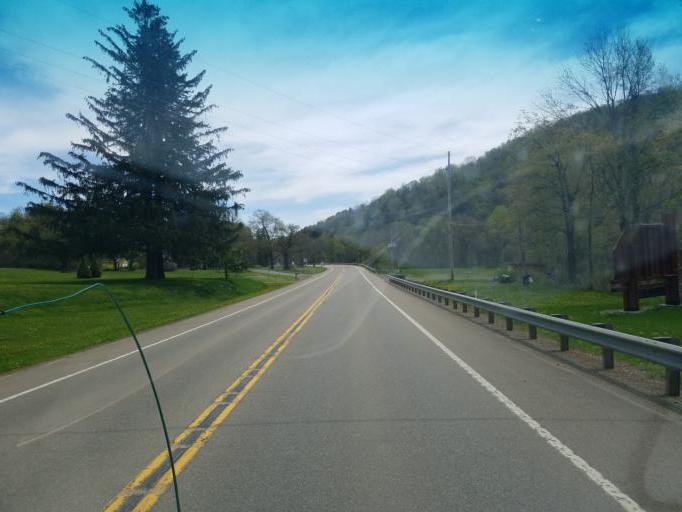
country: US
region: Pennsylvania
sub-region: Potter County
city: Galeton
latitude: 41.7390
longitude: -77.6255
